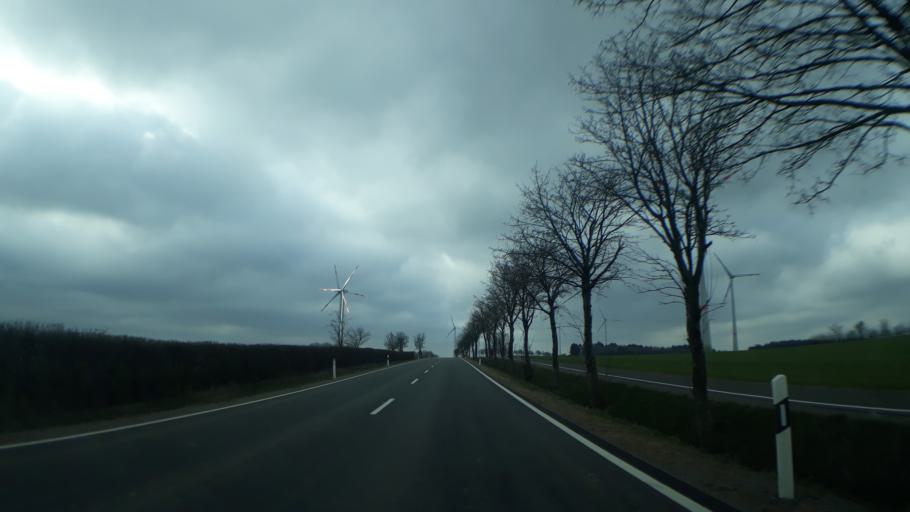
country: DE
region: North Rhine-Westphalia
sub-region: Regierungsbezirk Koln
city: Hellenthal
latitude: 50.5219
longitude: 6.3797
